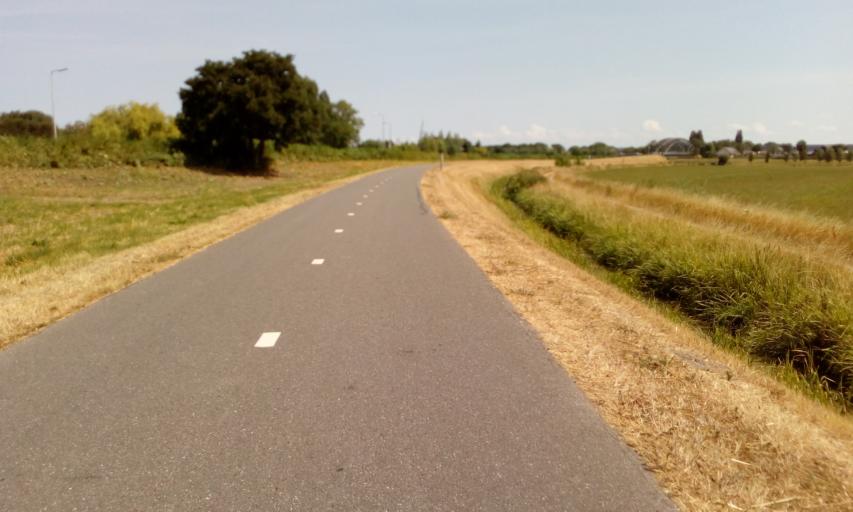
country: NL
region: South Holland
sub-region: Gemeente Westland
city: De Lier
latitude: 51.9699
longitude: 4.3058
